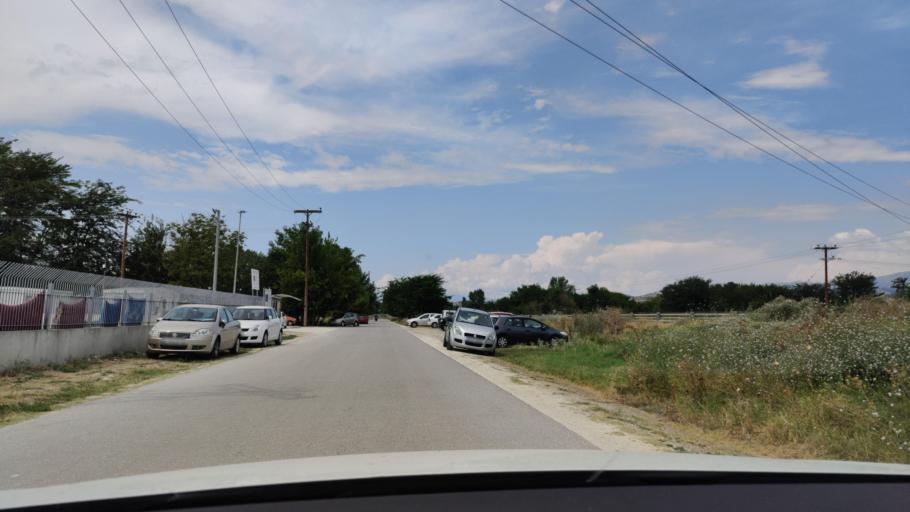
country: GR
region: Central Macedonia
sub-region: Nomos Serron
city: Serres
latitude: 41.0731
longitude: 23.5483
